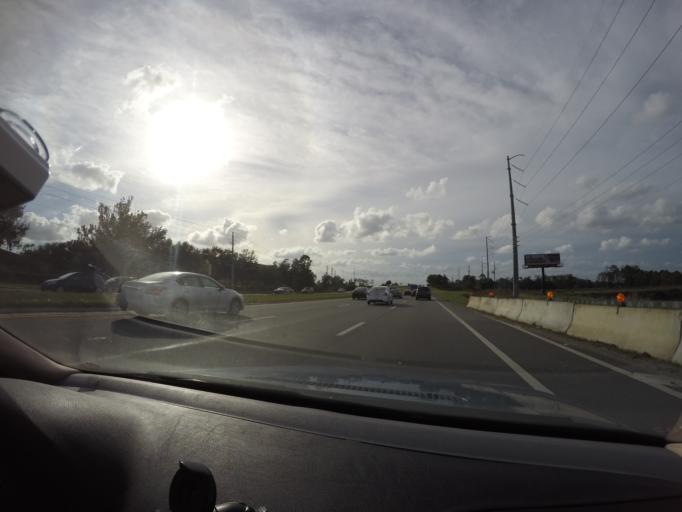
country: US
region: Florida
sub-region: Orange County
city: Oak Ridge
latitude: 28.4506
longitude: -81.4168
